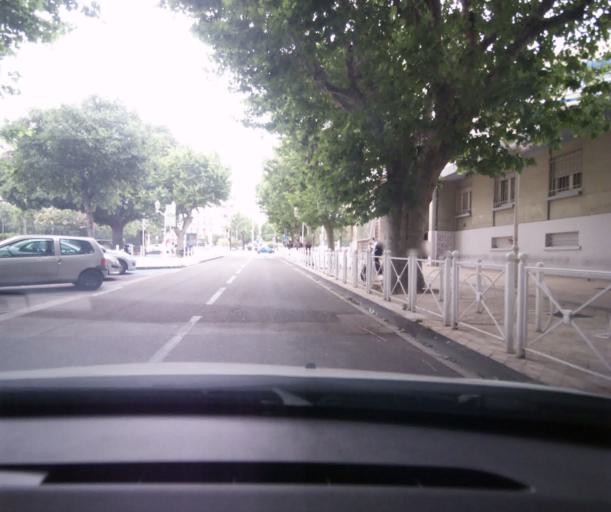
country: FR
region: Provence-Alpes-Cote d'Azur
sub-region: Departement du Var
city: Toulon
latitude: 43.1255
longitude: 5.9260
